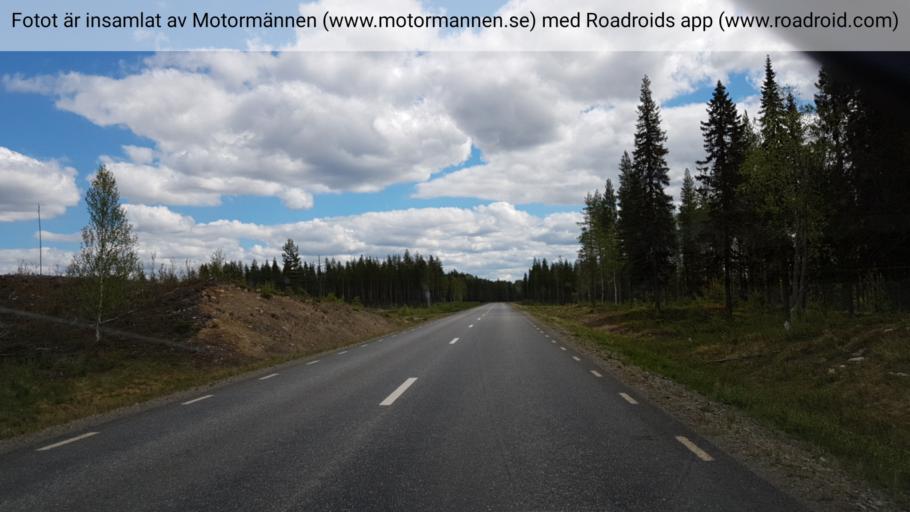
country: SE
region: Vaesterbotten
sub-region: Norsjo Kommun
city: Norsjoe
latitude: 64.8853
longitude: 19.6668
